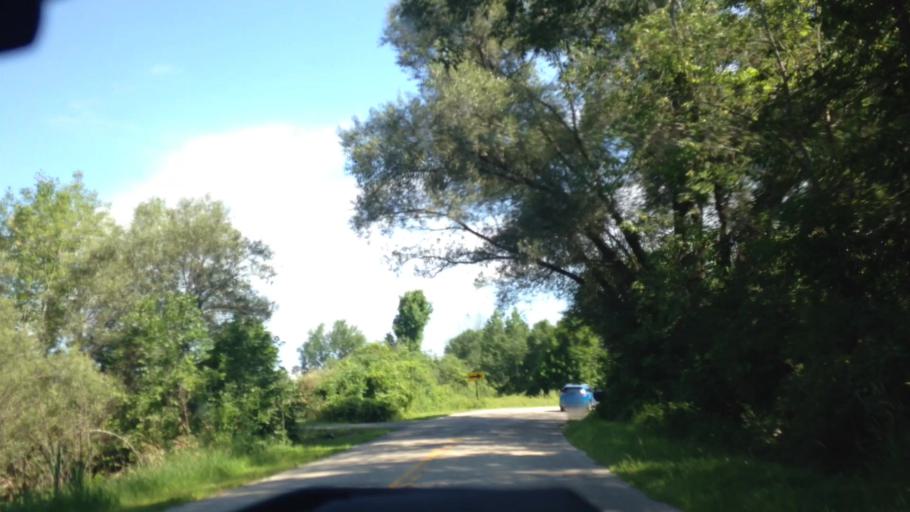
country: US
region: Wisconsin
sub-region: Washington County
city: West Bend
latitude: 43.4117
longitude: -88.2310
